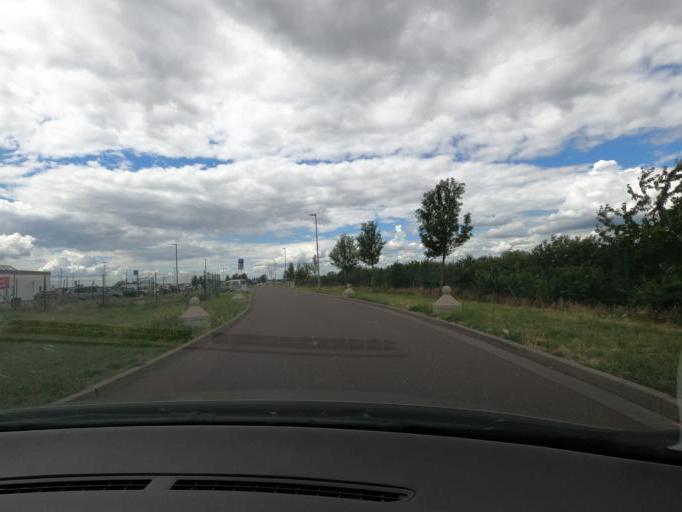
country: DE
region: Saxony-Anhalt
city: Gross Santersleben
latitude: 52.1848
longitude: 11.4548
